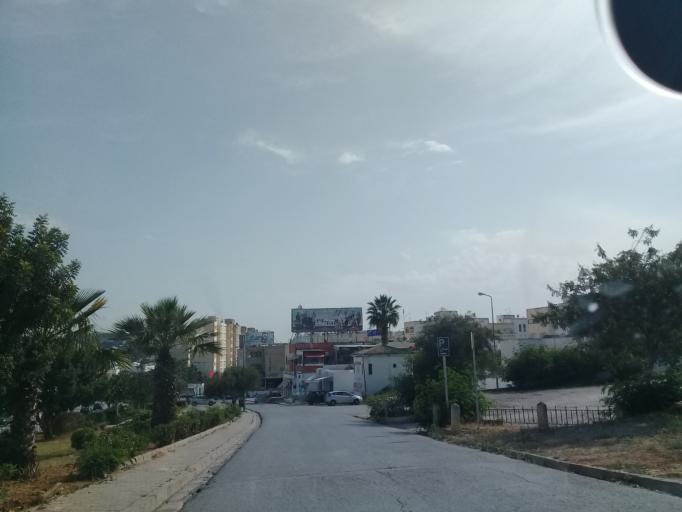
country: TN
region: Ariana
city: Ariana
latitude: 36.8479
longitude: 10.1681
